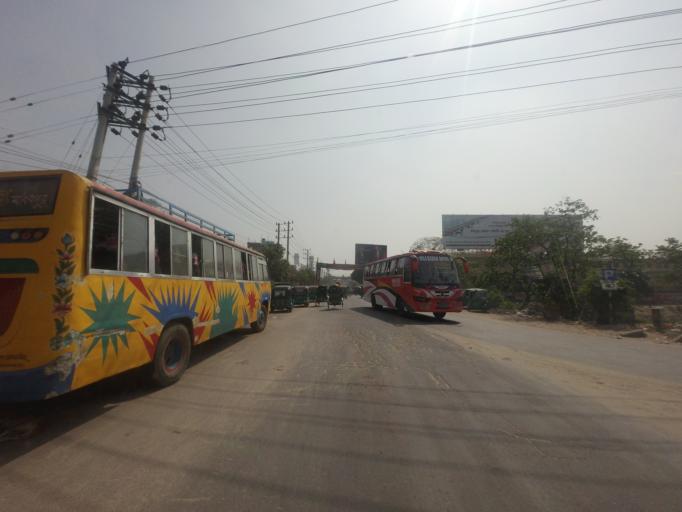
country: BD
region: Dhaka
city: Bhairab Bazar
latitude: 24.0385
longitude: 91.0041
